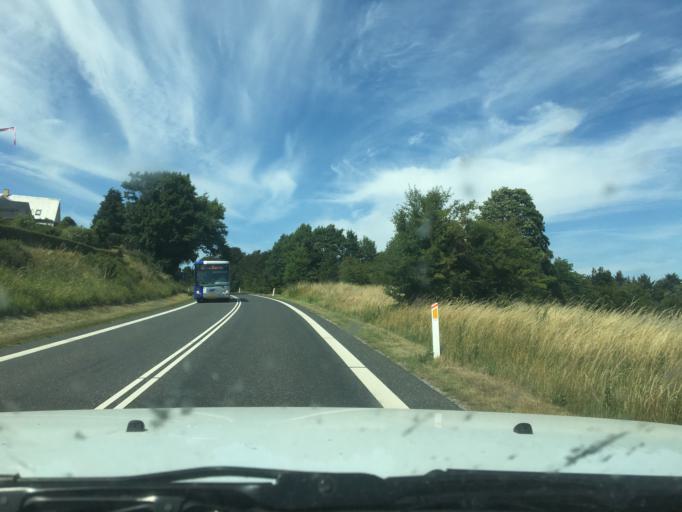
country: DK
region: Central Jutland
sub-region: Viborg Kommune
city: Viborg
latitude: 56.5764
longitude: 9.3773
